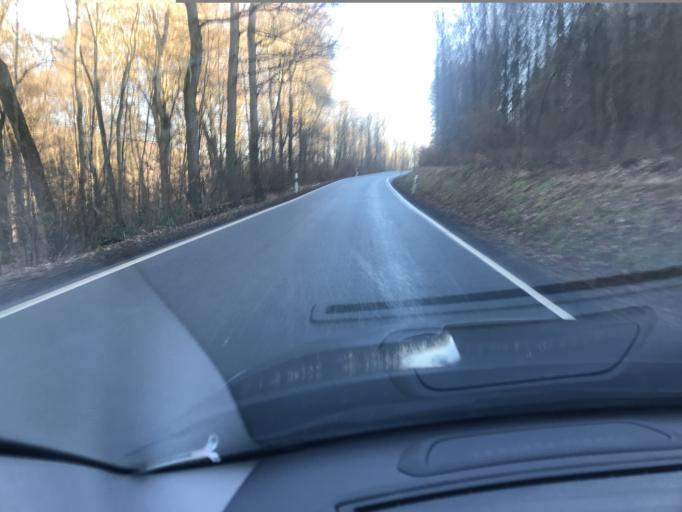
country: DE
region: Rheinland-Pfalz
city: Niedererbach
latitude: 50.4212
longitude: 7.9964
